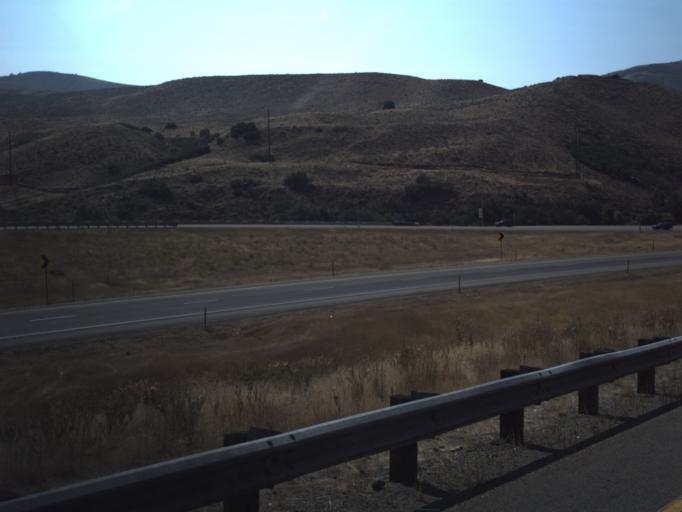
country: US
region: Utah
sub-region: Summit County
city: Coalville
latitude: 40.9717
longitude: -111.4389
